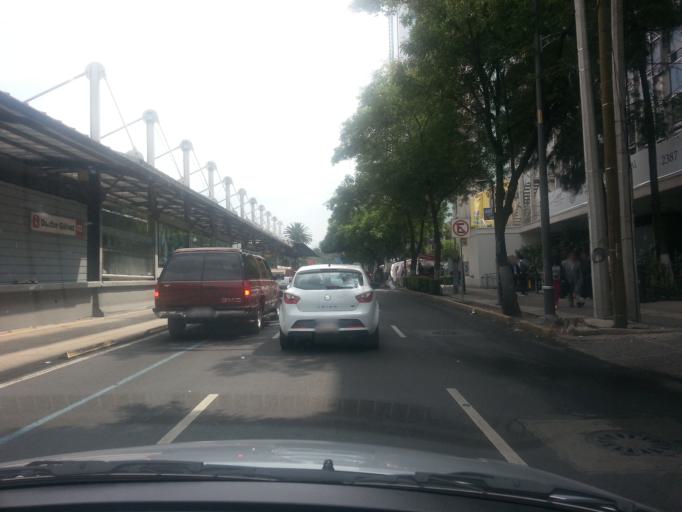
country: MX
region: Mexico City
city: Alvaro Obregon
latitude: 19.3413
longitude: -99.1899
